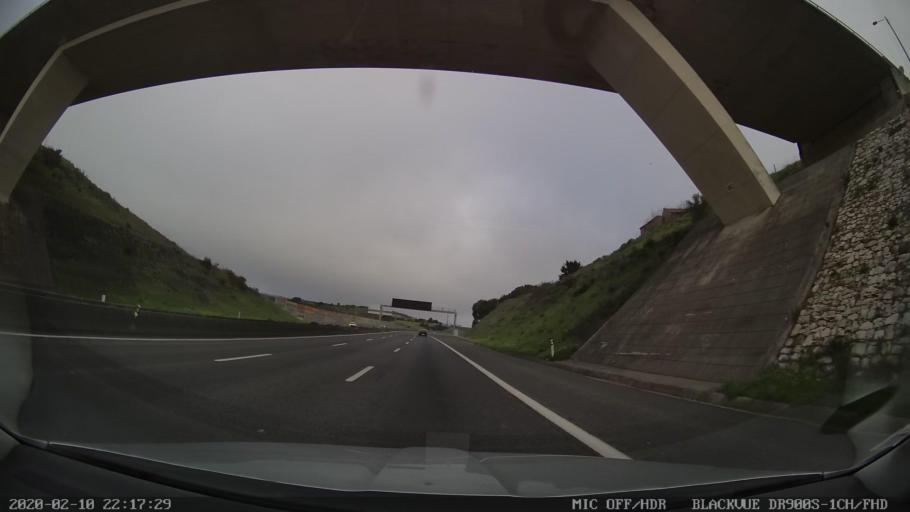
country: PT
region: Lisbon
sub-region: Vila Franca de Xira
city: Sobralinho
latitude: 38.9182
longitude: -9.0740
